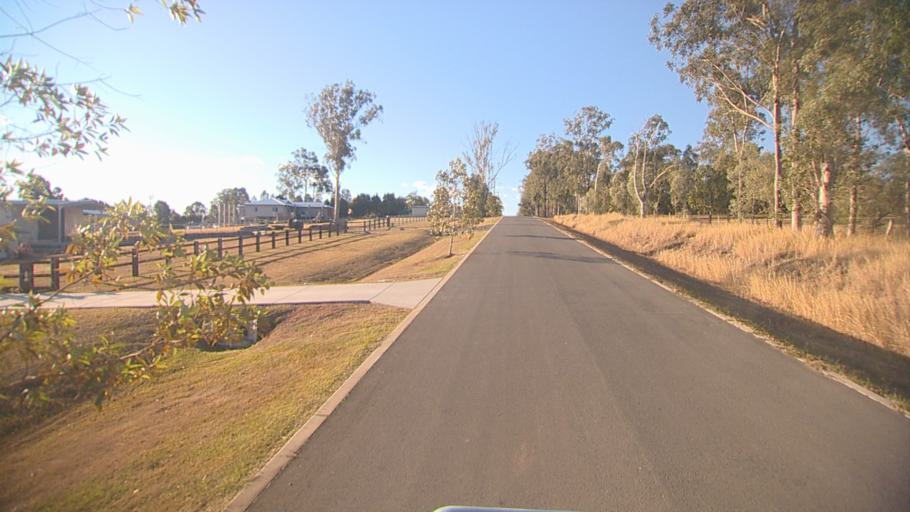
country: AU
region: Queensland
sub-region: Logan
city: Cedar Vale
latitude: -27.8737
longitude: 152.9742
